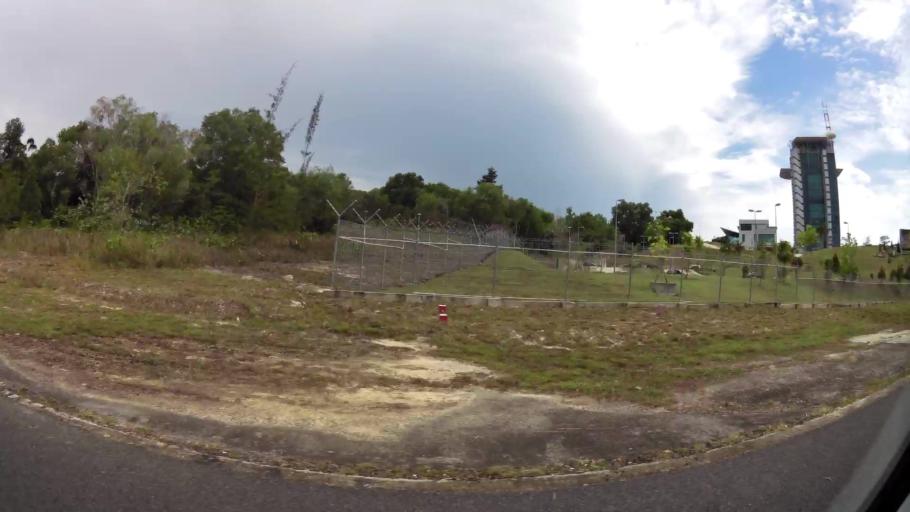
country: BN
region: Brunei and Muara
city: Bandar Seri Begawan
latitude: 4.9653
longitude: 114.8877
